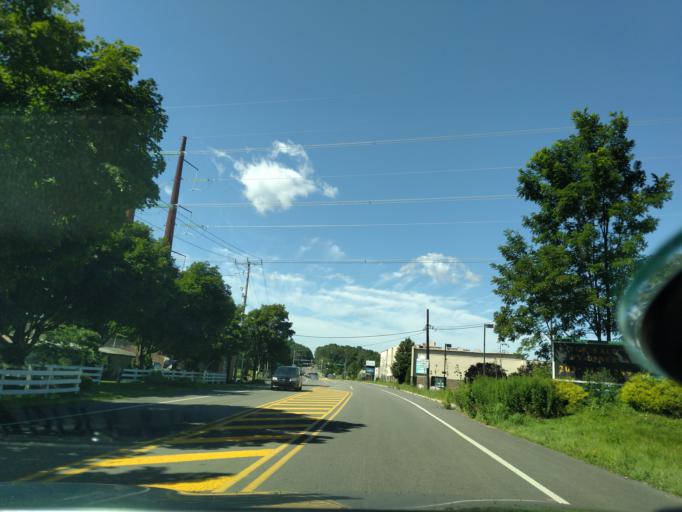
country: US
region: Pennsylvania
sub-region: Pike County
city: Saw Creek
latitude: 41.0803
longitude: -75.0239
